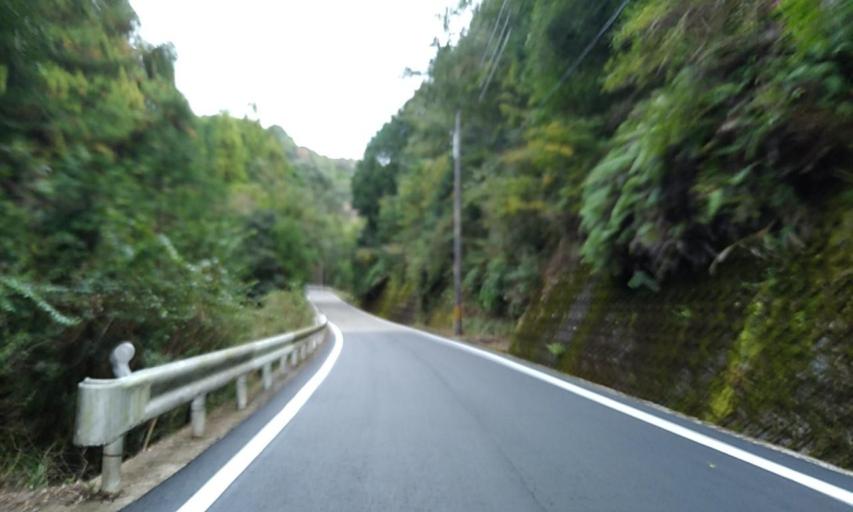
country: JP
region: Wakayama
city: Shingu
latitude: 33.5423
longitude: 135.8406
